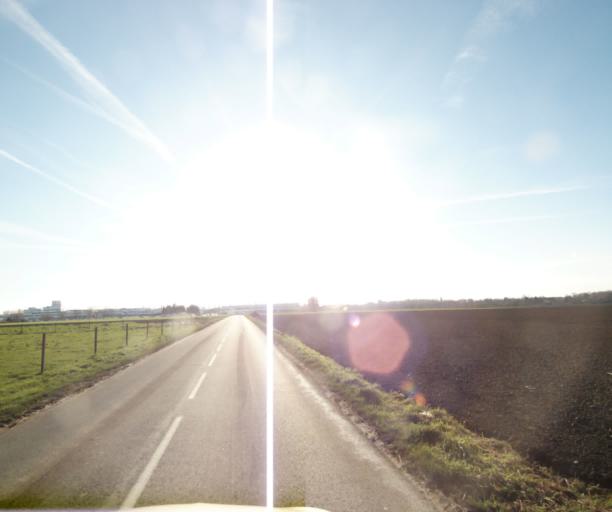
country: FR
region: Nord-Pas-de-Calais
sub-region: Departement du Nord
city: Saultain
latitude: 50.3447
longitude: 3.5891
